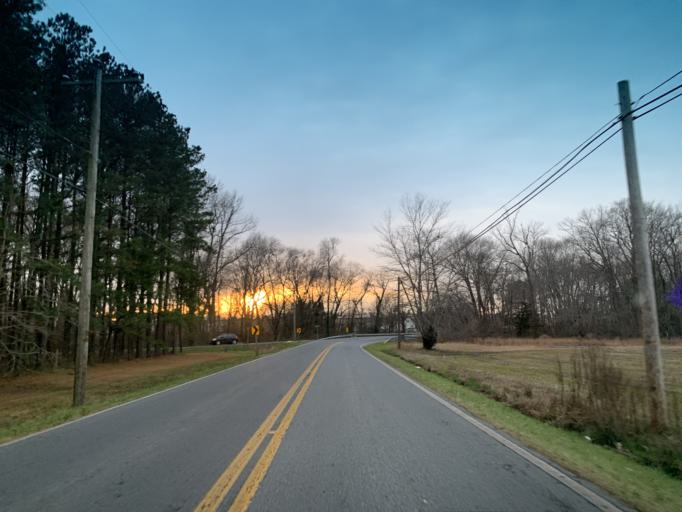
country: US
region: Maryland
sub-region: Worcester County
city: Pocomoke City
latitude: 38.0753
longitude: -75.5517
